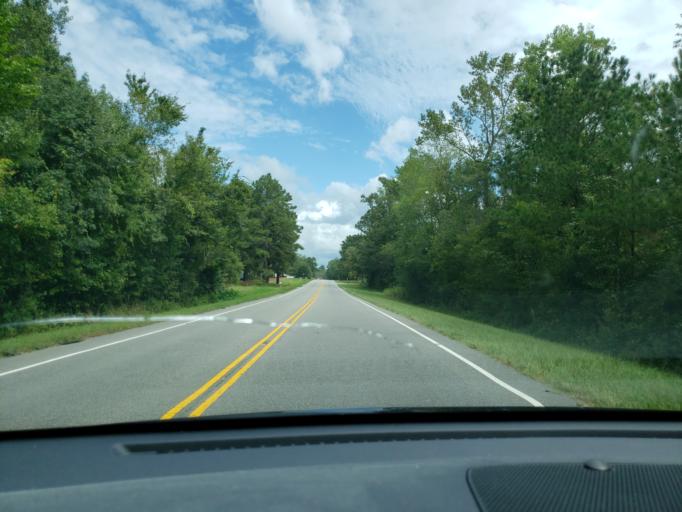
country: US
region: North Carolina
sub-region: Columbus County
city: Tabor City
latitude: 34.1910
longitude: -78.7719
